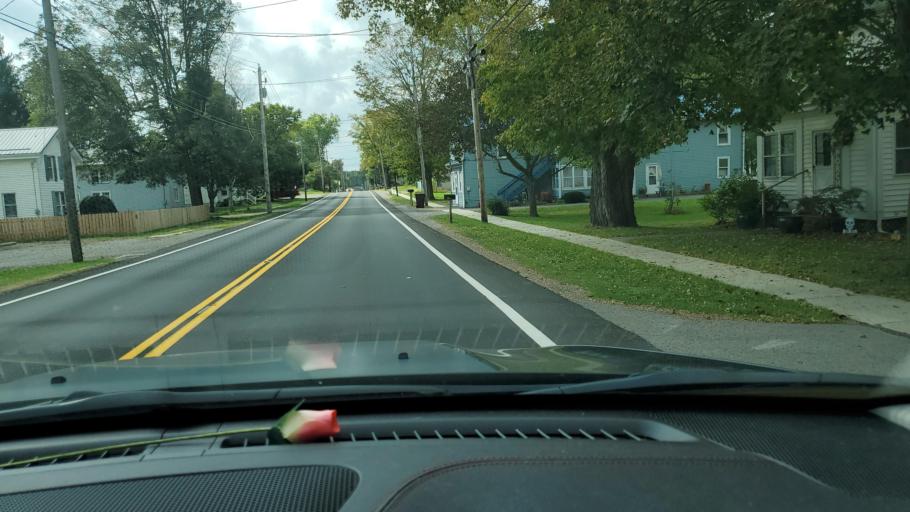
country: US
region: Ohio
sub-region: Ashtabula County
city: Andover
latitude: 41.4503
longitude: -80.5838
